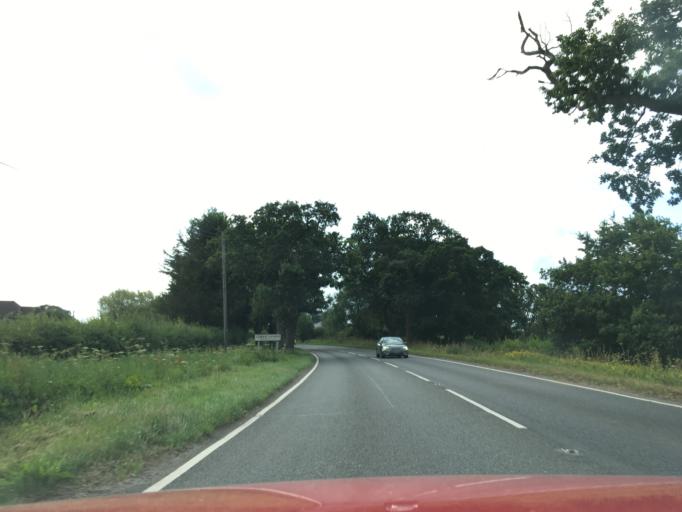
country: GB
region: England
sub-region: Hampshire
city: Colden Common
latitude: 50.9770
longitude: -1.2642
